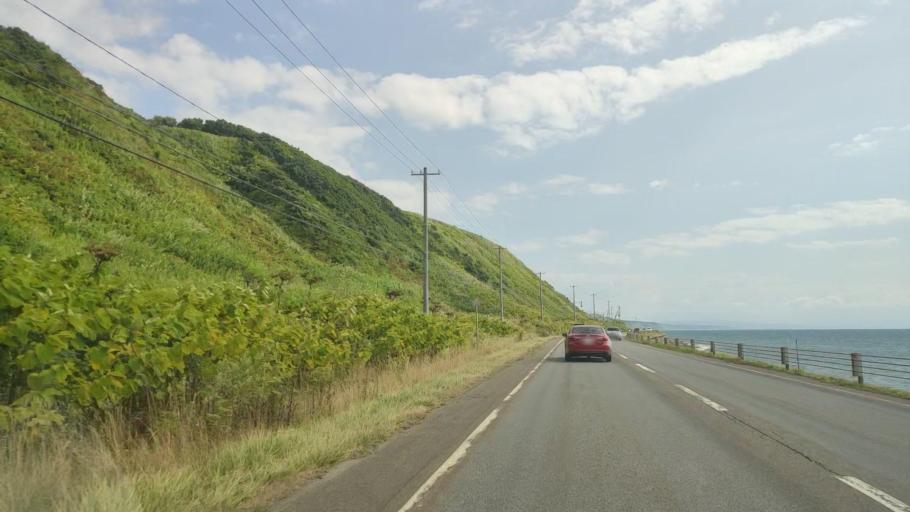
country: JP
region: Hokkaido
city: Rumoi
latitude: 44.0939
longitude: 141.6609
